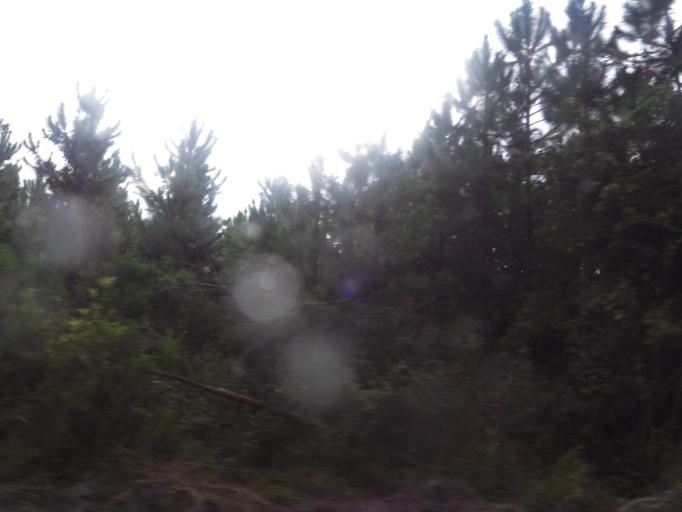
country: US
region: Florida
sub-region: Flagler County
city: Bunnell
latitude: 29.5653
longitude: -81.3354
